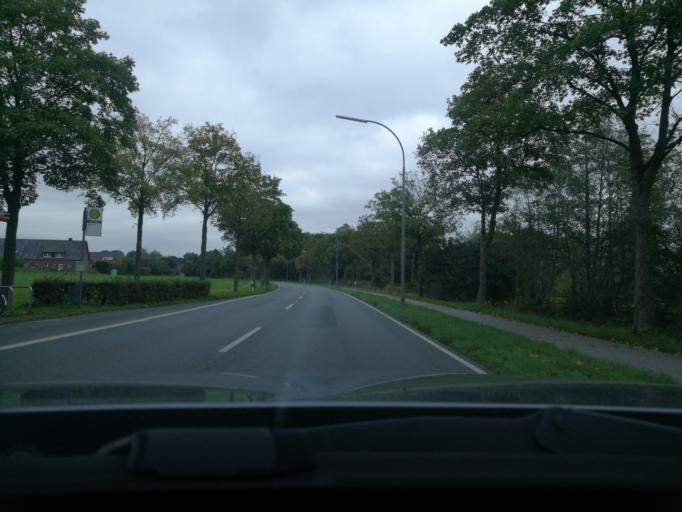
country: DE
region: North Rhine-Westphalia
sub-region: Regierungsbezirk Dusseldorf
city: Kevelaer
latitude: 51.5294
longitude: 6.2426
